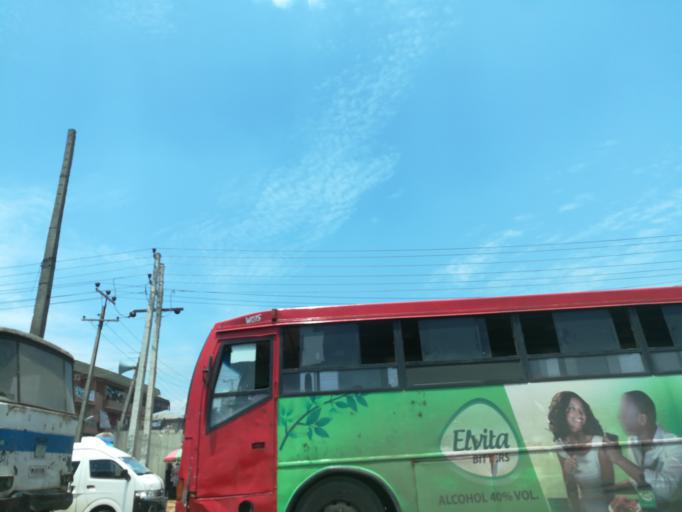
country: NG
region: Lagos
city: Ikorodu
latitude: 6.6220
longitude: 3.5042
